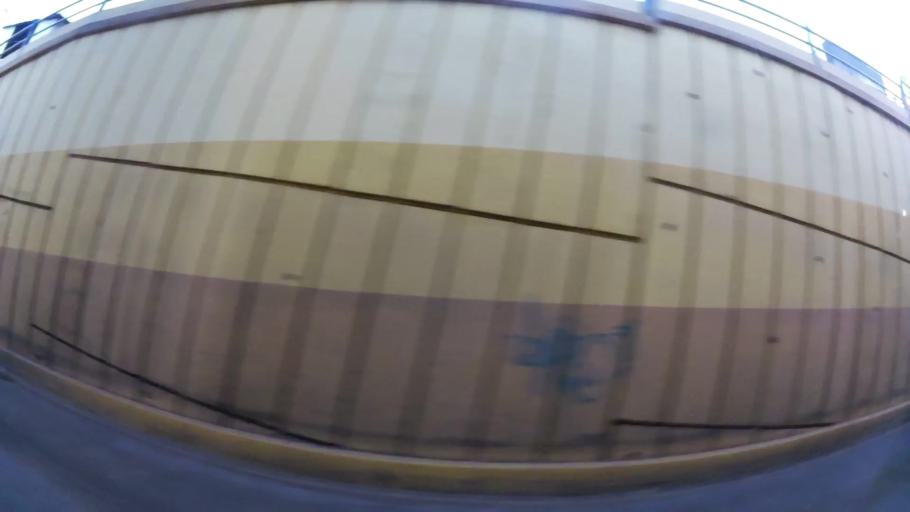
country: EC
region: Tungurahua
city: Ambato
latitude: -1.2474
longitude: -78.6315
